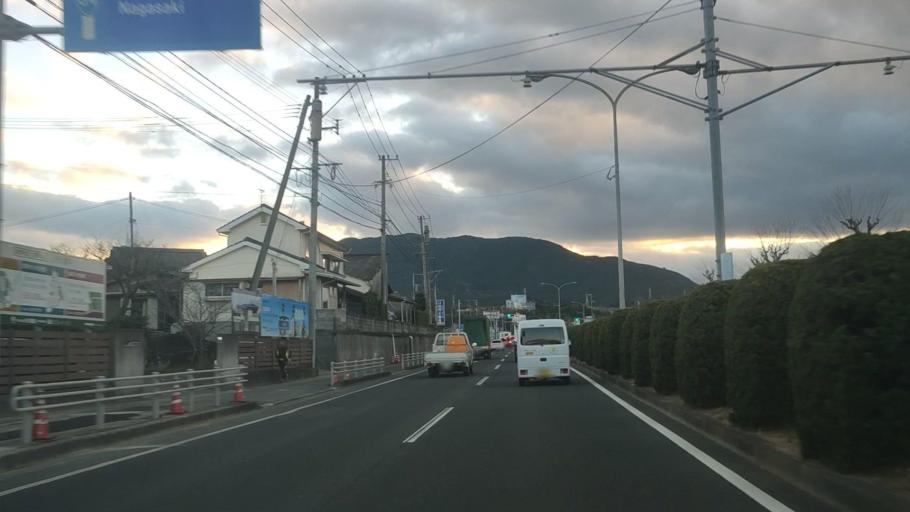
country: JP
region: Nagasaki
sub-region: Isahaya-shi
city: Isahaya
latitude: 32.8346
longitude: 130.0034
